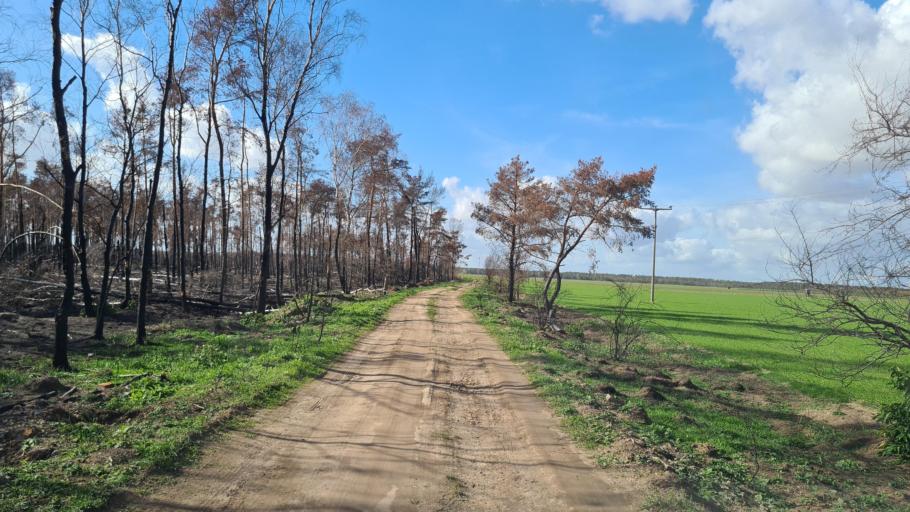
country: DE
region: Saxony
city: Nauwalde
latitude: 51.4375
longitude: 13.3276
